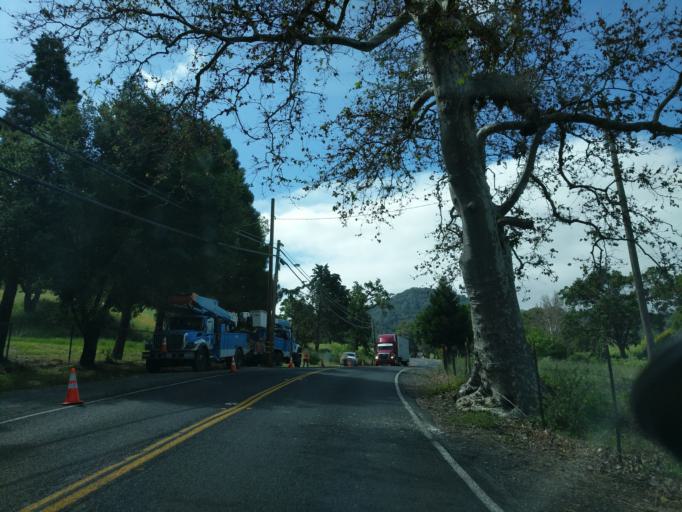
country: US
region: California
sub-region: Contra Costa County
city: Clayton
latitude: 37.8992
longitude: -121.8609
